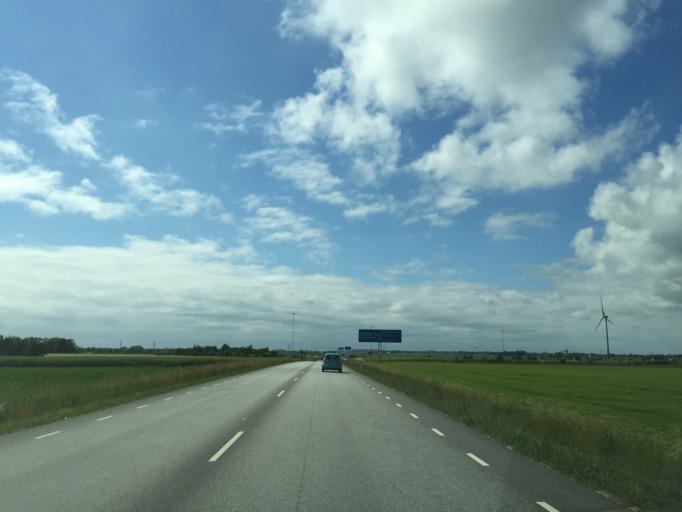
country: SE
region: Skane
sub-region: Staffanstorps Kommun
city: Hjaerup
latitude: 55.6941
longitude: 13.1401
